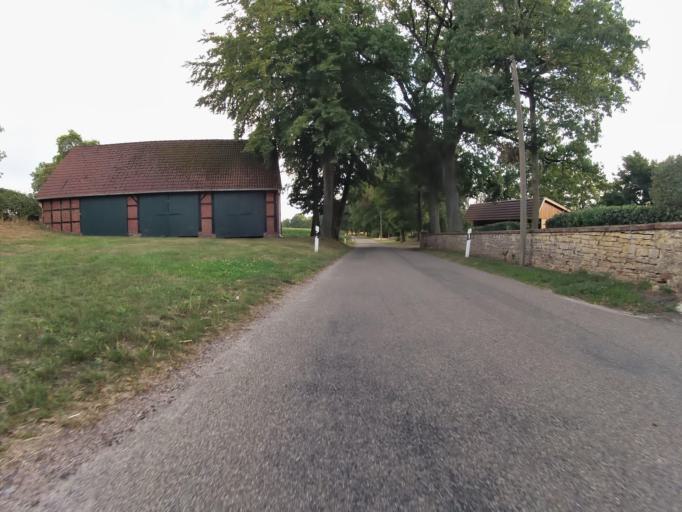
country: DE
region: North Rhine-Westphalia
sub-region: Regierungsbezirk Munster
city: Westerkappeln
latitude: 52.3650
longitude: 7.8785
